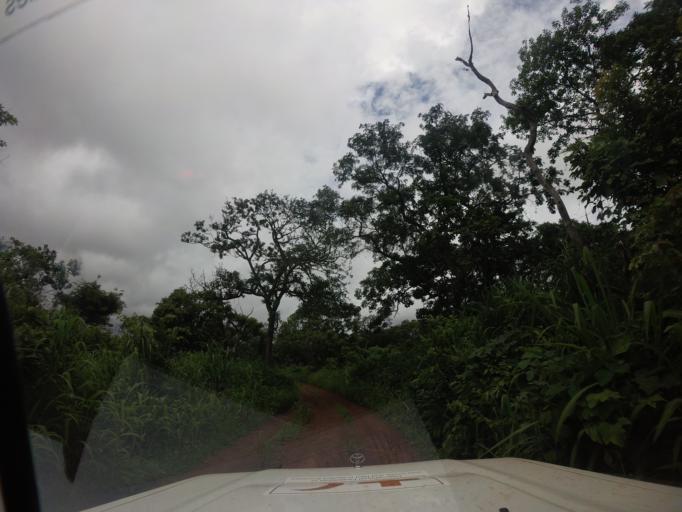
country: SL
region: Northern Province
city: Kamakwie
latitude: 9.6834
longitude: -12.2485
